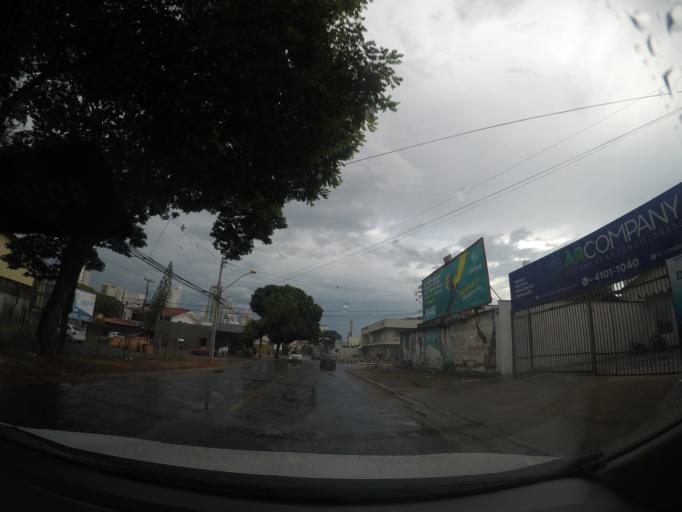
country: BR
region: Goias
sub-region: Goiania
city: Goiania
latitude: -16.7108
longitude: -49.2756
